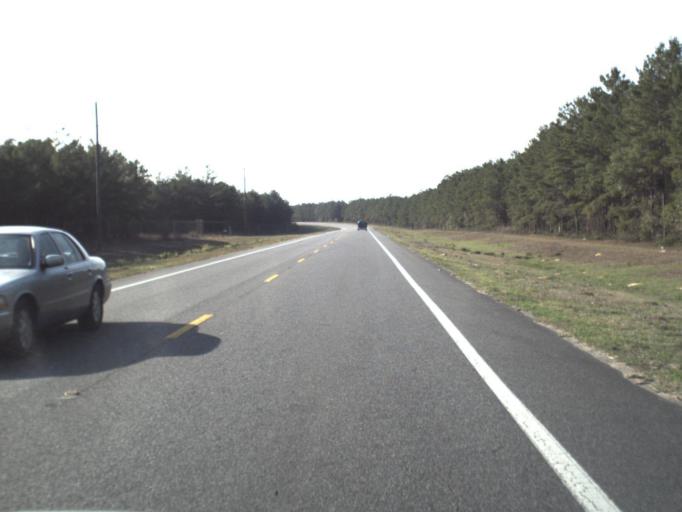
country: US
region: Florida
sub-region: Bay County
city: Lynn Haven
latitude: 30.4364
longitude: -85.6981
